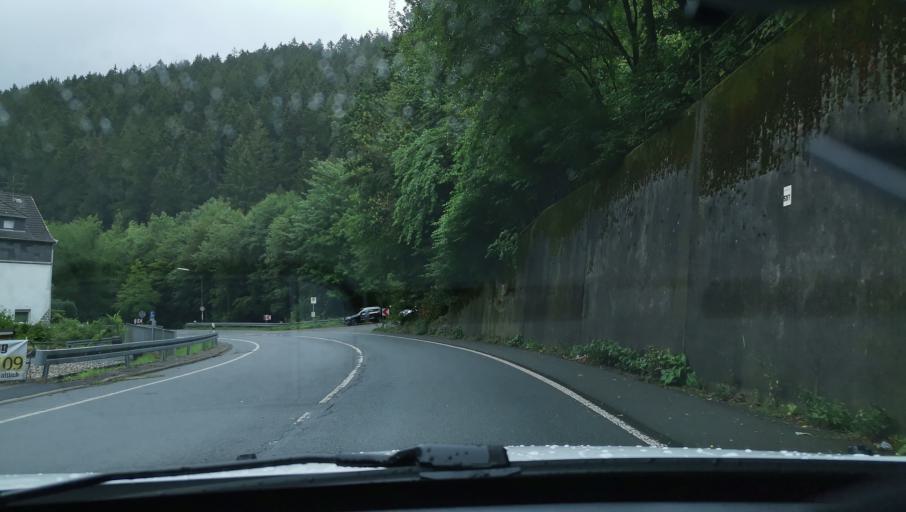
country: DE
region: North Rhine-Westphalia
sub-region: Regierungsbezirk Arnsberg
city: Schalksmuhle
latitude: 51.2260
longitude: 7.5323
